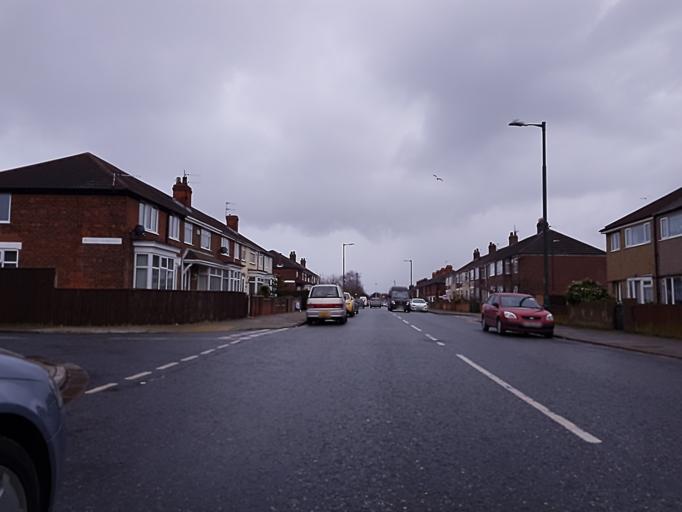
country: GB
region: England
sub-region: North East Lincolnshire
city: Grimbsy
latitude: 53.5679
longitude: -0.1082
